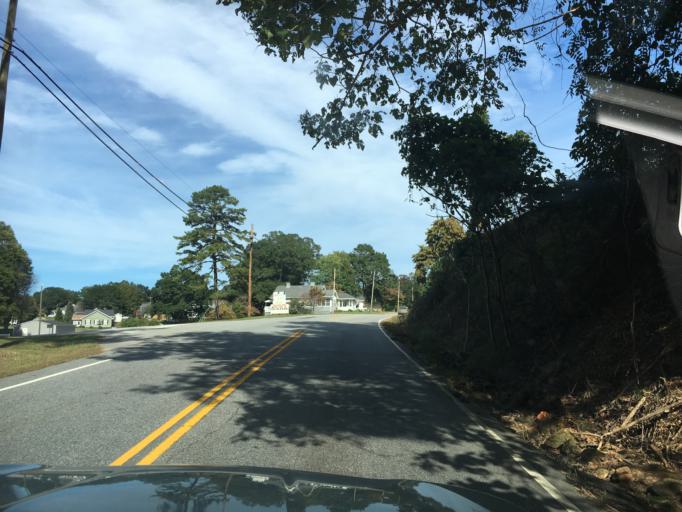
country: US
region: South Carolina
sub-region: Spartanburg County
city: Lyman
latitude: 34.9473
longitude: -82.1287
